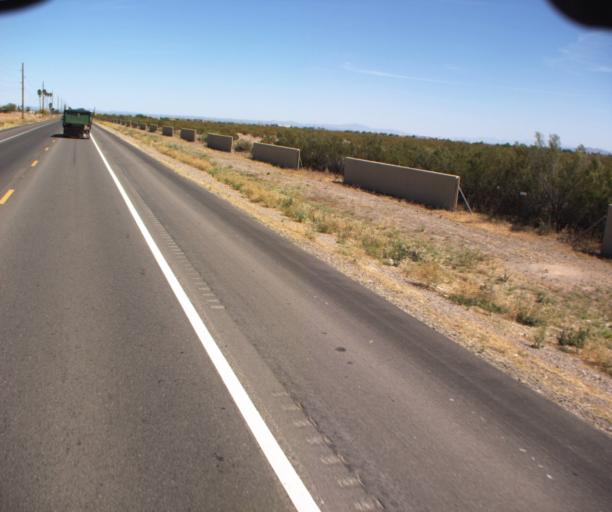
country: US
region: Arizona
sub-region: Pinal County
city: Coolidge
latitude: 33.0025
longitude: -111.5378
